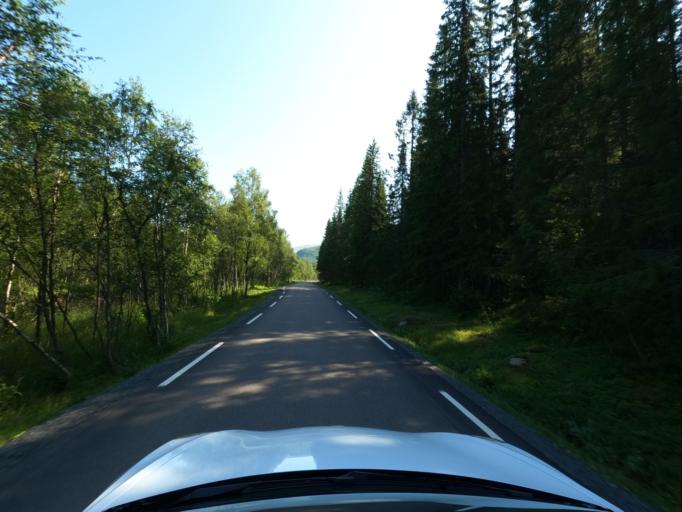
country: NO
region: Nordland
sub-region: Narvik
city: Narvik
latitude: 68.3911
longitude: 17.3386
